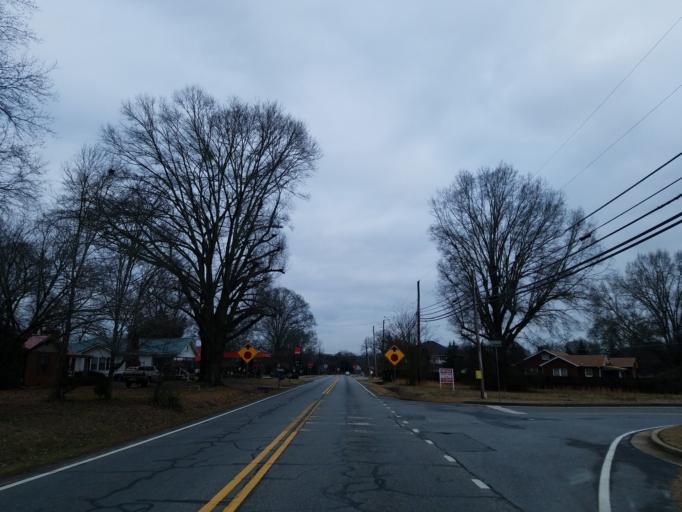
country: US
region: Georgia
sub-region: Bartow County
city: Cartersville
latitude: 34.1915
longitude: -84.8210
